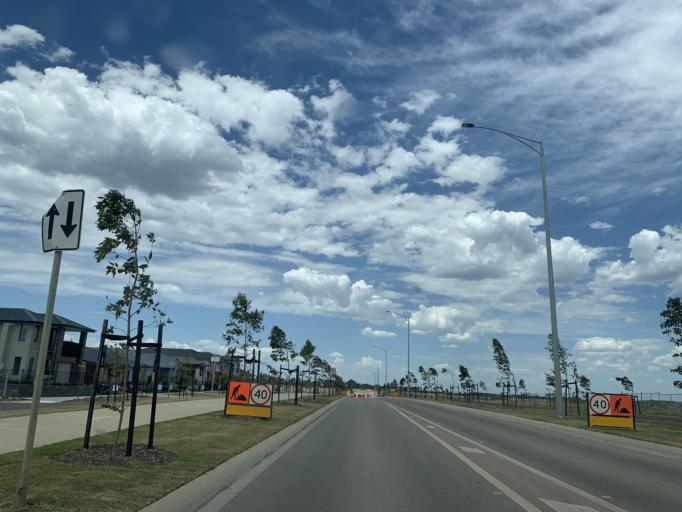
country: AU
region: Victoria
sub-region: Cardinia
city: Officer South
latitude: -38.1236
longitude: 145.3678
